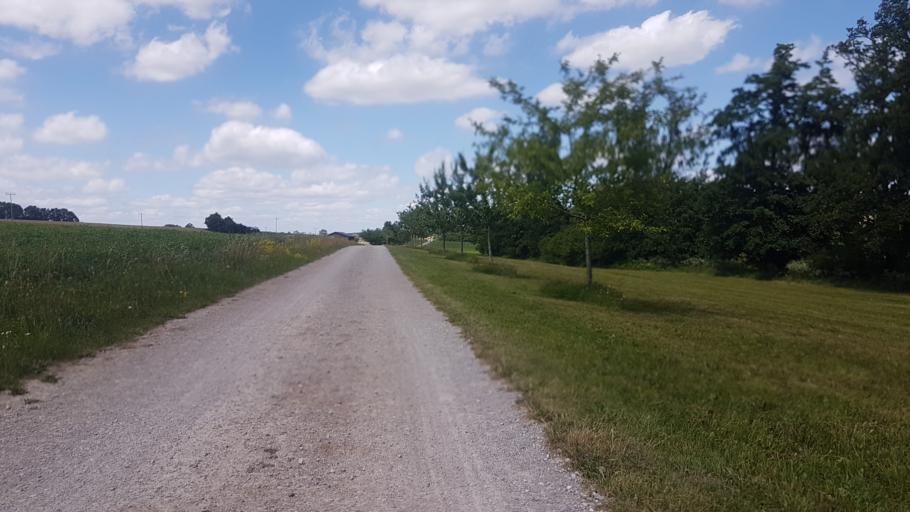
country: DE
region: Bavaria
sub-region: Regierungsbezirk Mittelfranken
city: Leutershausen
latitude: 49.3154
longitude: 10.3880
